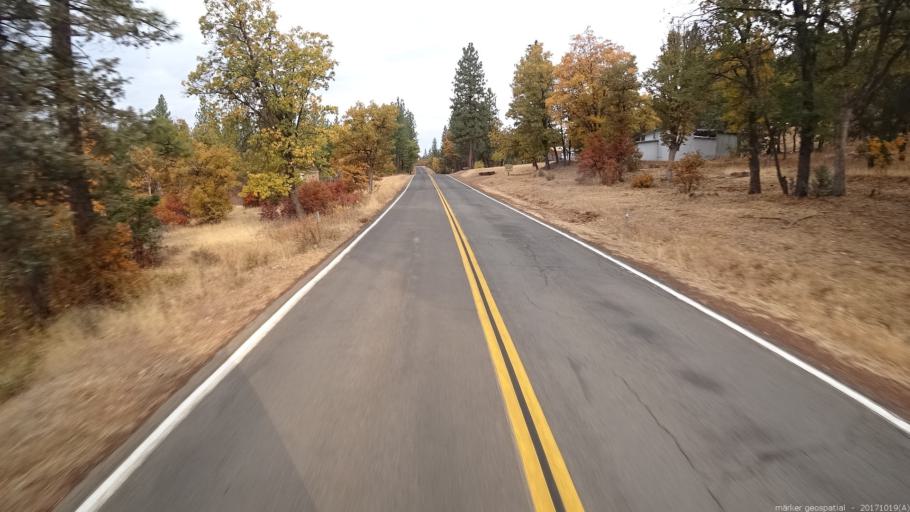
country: US
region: California
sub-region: Shasta County
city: Burney
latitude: 41.1551
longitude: -121.3541
